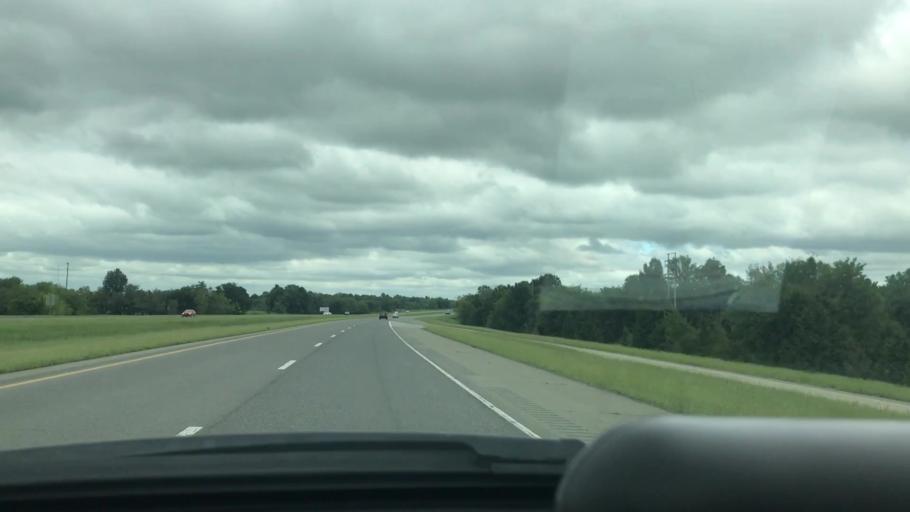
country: US
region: Oklahoma
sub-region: McIntosh County
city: Checotah
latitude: 35.5788
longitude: -95.4907
